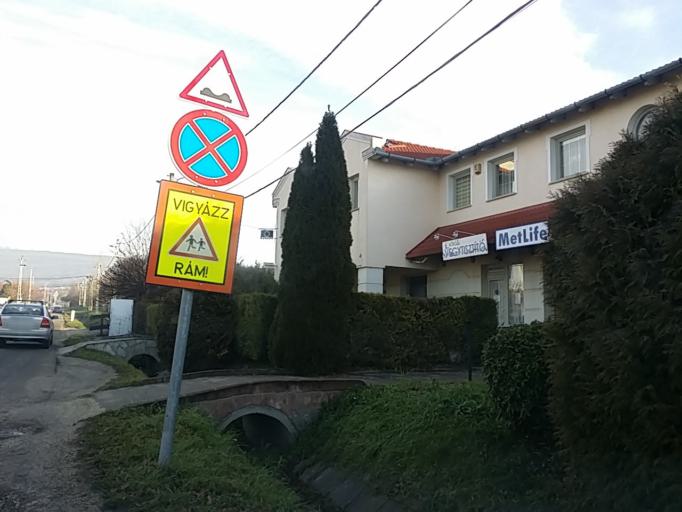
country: HU
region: Pest
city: Telki
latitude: 47.5511
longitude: 18.8207
